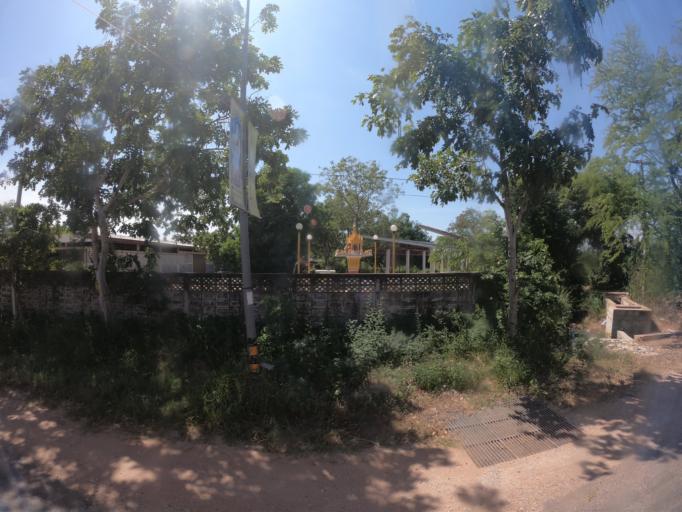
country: TH
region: Khon Kaen
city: Ban Phai
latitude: 16.0655
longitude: 102.7227
